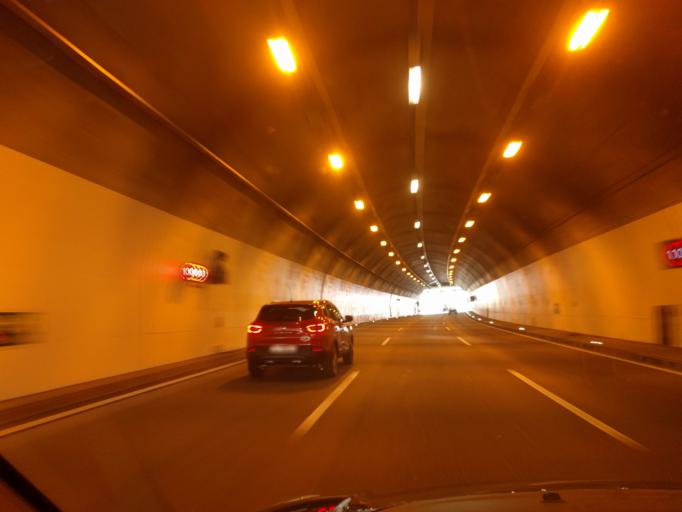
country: CH
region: Ticino
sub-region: Leventina District
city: Faido
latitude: 46.4841
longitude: 8.7782
